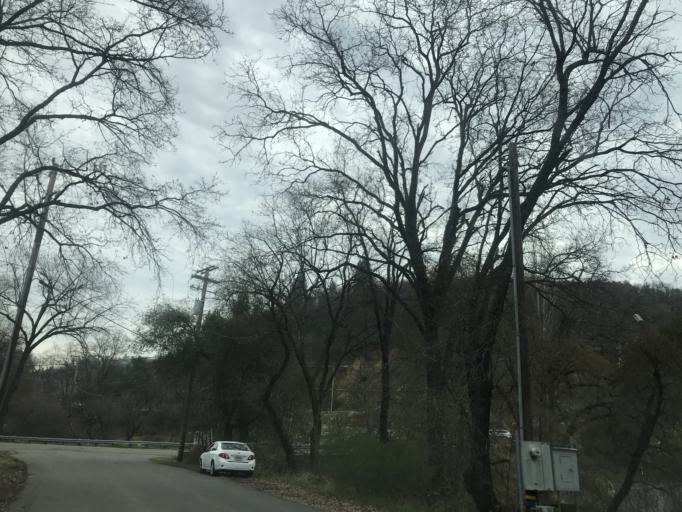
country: US
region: California
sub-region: El Dorado County
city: Placerville
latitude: 38.7343
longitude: -120.8305
